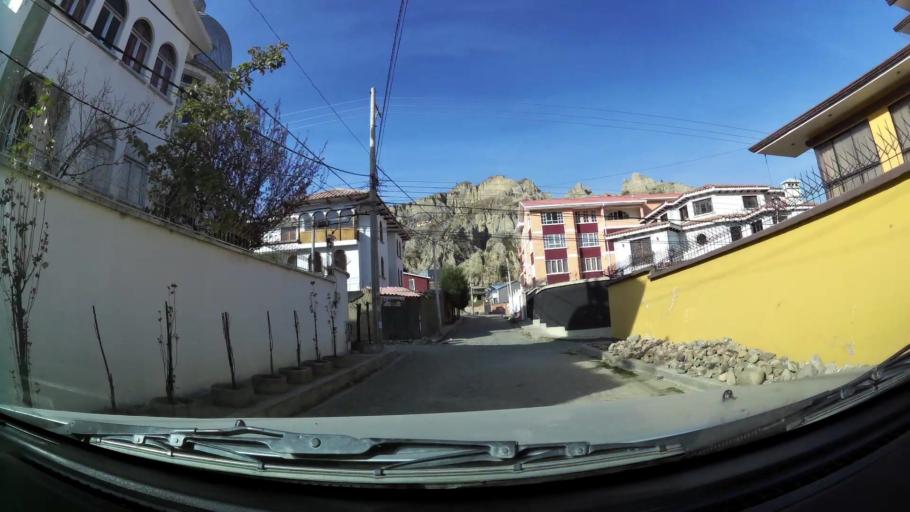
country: BO
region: La Paz
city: La Paz
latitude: -16.5000
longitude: -68.0834
